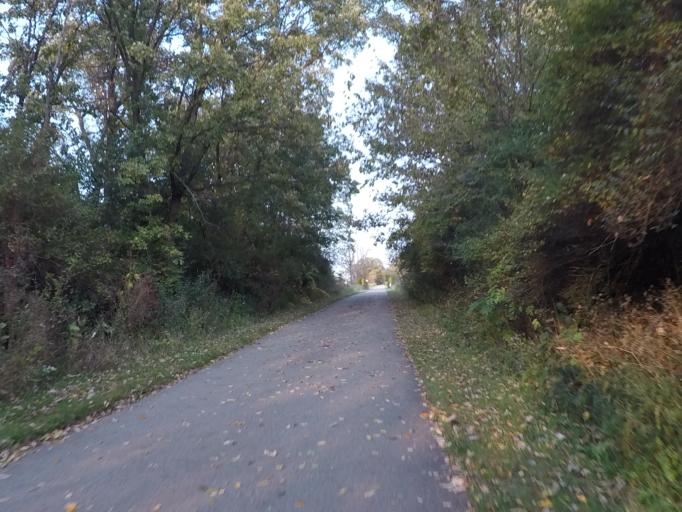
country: US
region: Wisconsin
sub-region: Dane County
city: Verona
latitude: 42.9975
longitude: -89.4983
